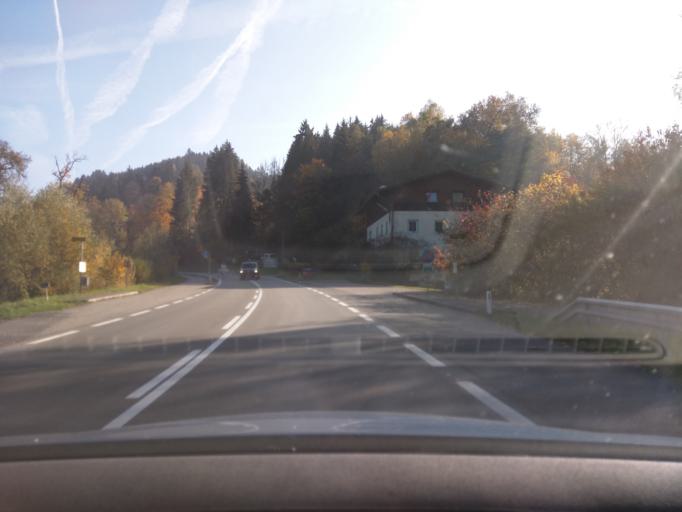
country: DE
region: Bavaria
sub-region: Lower Bavaria
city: Thyrnau
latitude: 48.5684
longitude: 13.5485
